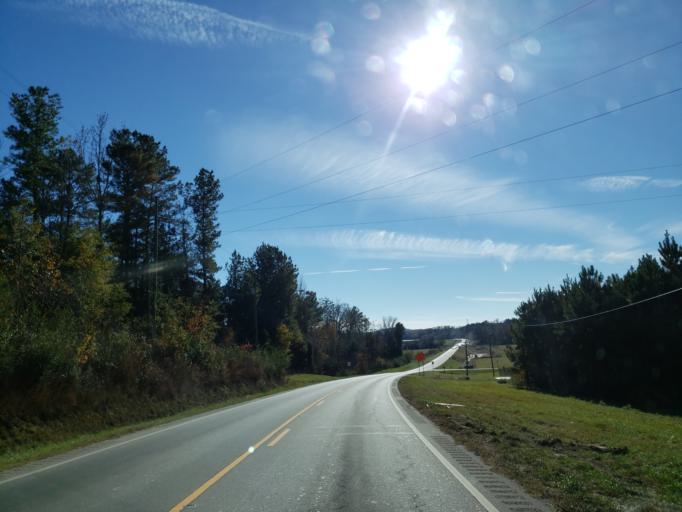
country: US
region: Alabama
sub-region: Cleburne County
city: Heflin
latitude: 33.6110
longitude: -85.5980
